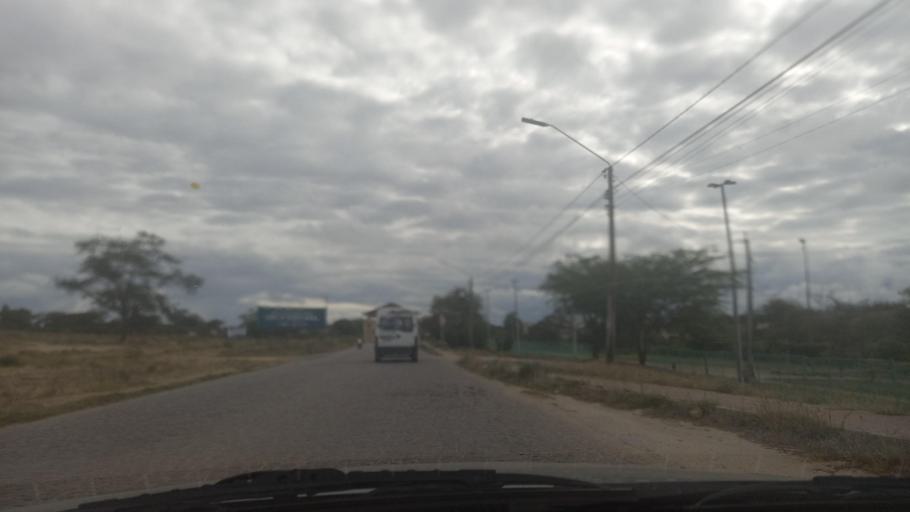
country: BR
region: Pernambuco
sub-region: Caruaru
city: Caruaru
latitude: -8.2894
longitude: -36.0238
